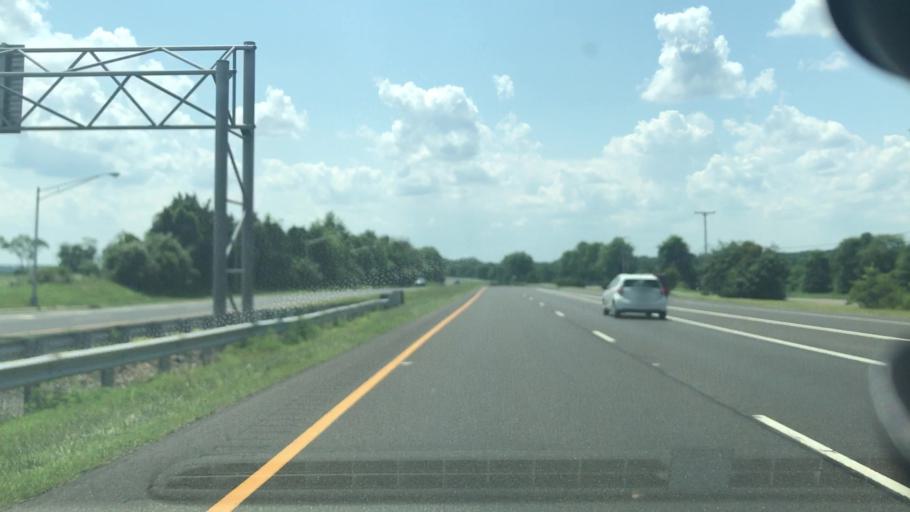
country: US
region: New Jersey
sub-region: Hunterdon County
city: Lambertville
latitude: 40.4173
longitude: -74.8810
